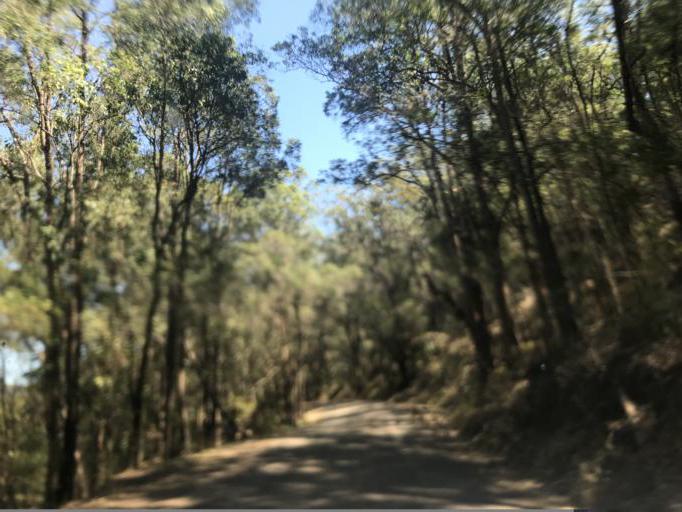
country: AU
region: New South Wales
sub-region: Wyong Shire
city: Little Jilliby
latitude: -33.1962
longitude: 151.0098
